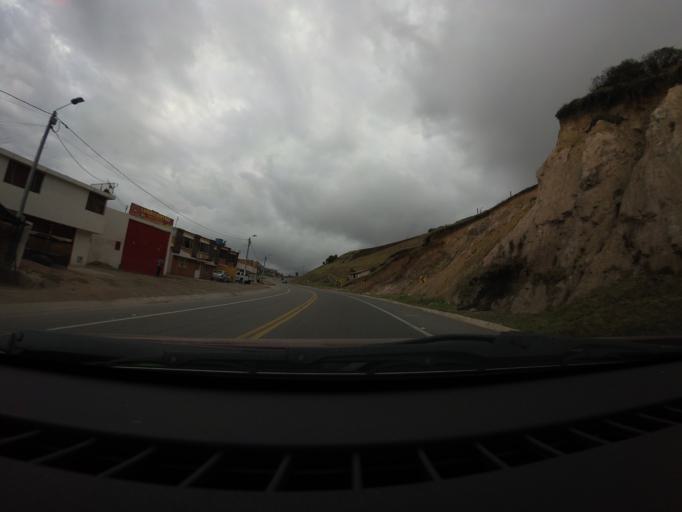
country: CO
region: Boyaca
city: Tunja
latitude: 5.4957
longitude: -73.3819
